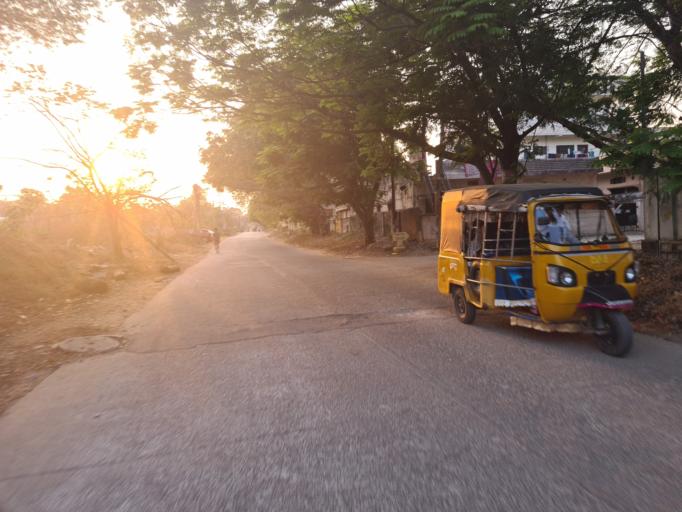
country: IN
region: Telangana
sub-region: Medak
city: Serilingampalle
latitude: 17.4815
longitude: 78.3091
